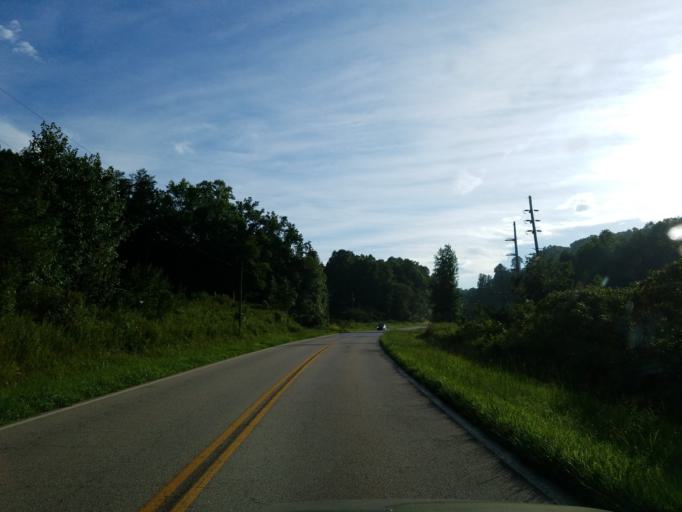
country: US
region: Georgia
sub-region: Lumpkin County
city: Dahlonega
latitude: 34.5248
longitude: -83.9088
